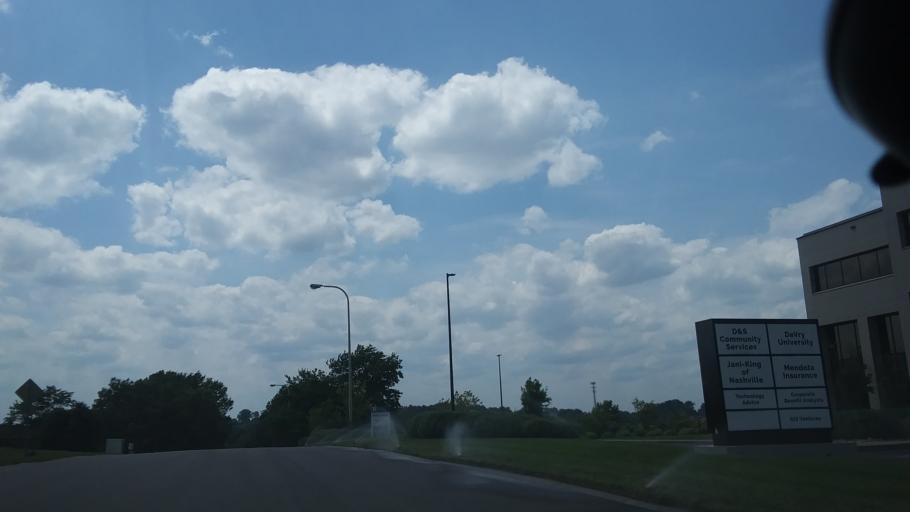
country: US
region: Tennessee
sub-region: Davidson County
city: Oak Hill
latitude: 36.0849
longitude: -86.6942
